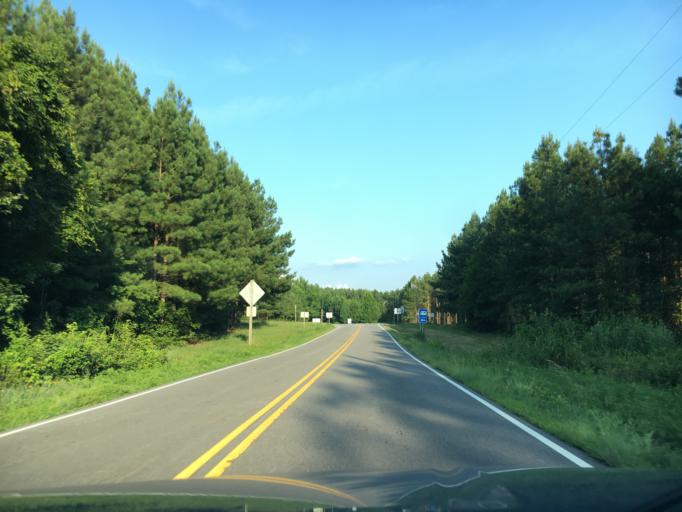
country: US
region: Virginia
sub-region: Pittsylvania County
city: Chatham
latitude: 36.8135
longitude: -79.2648
